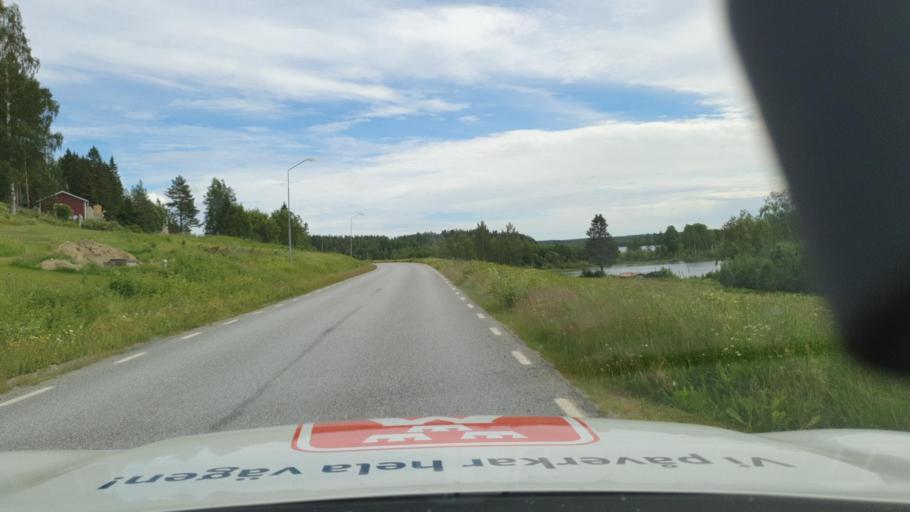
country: SE
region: Vaesterbotten
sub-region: Skelleftea Kommun
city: Burea
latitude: 64.4937
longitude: 21.0226
